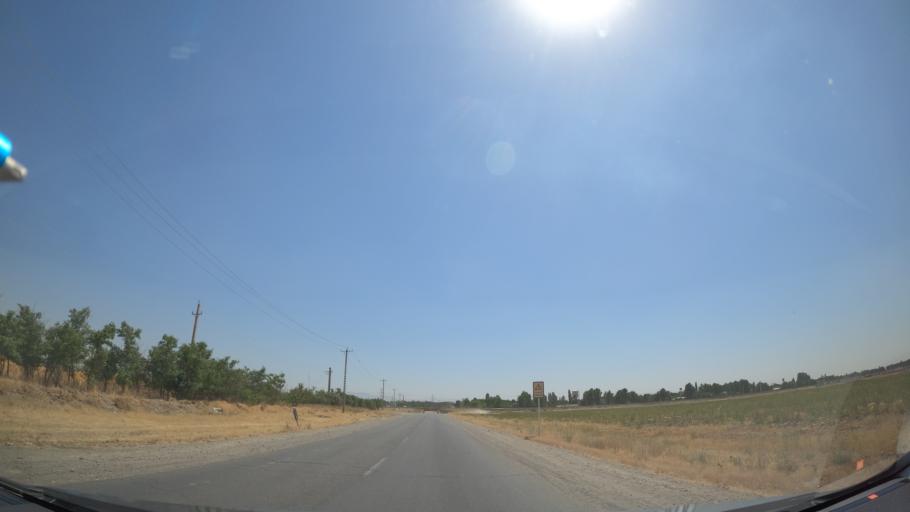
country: IR
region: Alborz
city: Hashtgerd
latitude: 35.9171
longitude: 50.7354
